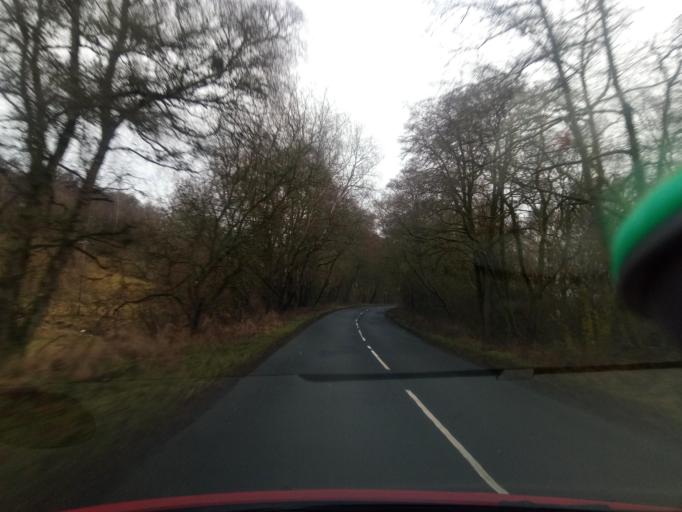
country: GB
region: England
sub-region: Northumberland
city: Rochester
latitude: 55.1552
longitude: -2.2918
